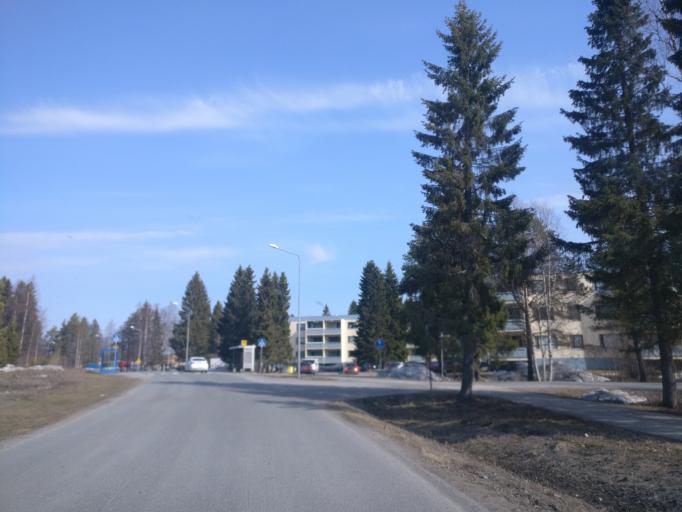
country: FI
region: Lapland
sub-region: Kemi-Tornio
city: Kemi
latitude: 65.7283
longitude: 24.6259
